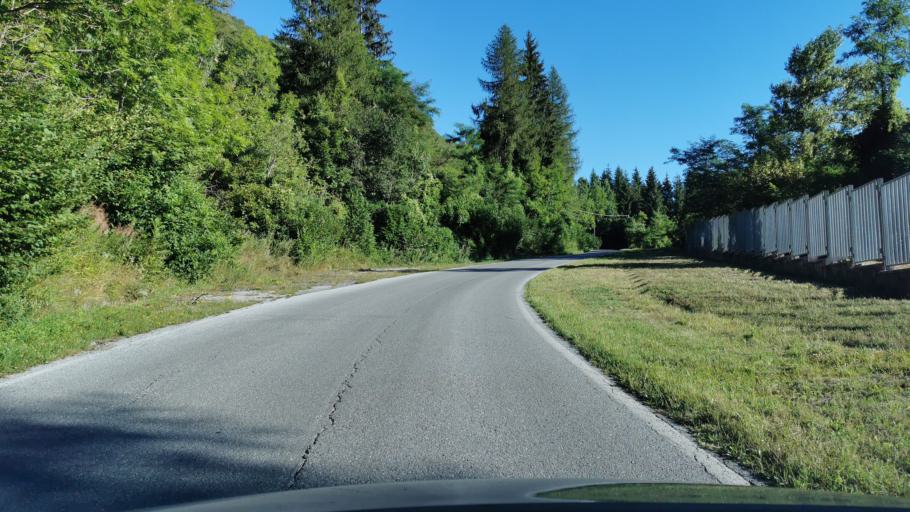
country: IT
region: Piedmont
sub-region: Provincia di Cuneo
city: Entracque
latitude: 44.2277
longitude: 7.3898
